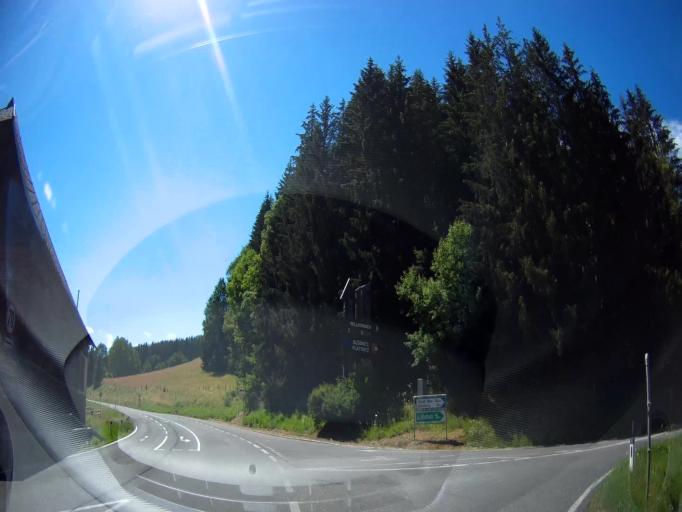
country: AT
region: Carinthia
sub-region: Politischer Bezirk Sankt Veit an der Glan
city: Glodnitz
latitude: 46.8531
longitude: 14.1379
